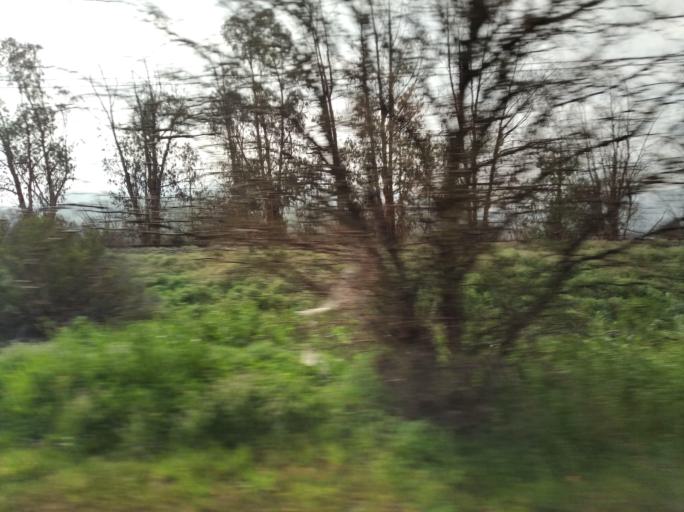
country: CL
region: Santiago Metropolitan
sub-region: Provincia de Chacabuco
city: Lampa
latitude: -33.1201
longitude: -70.9253
